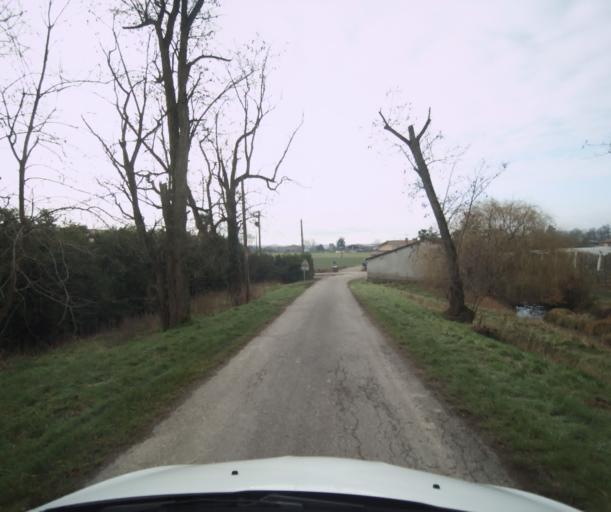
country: FR
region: Midi-Pyrenees
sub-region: Departement du Tarn-et-Garonne
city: Saint-Porquier
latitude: 44.0232
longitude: 1.1616
